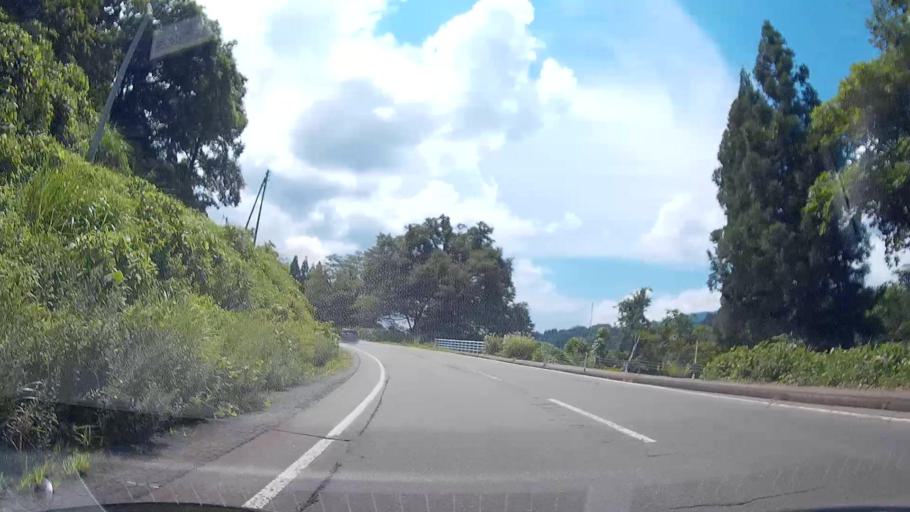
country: JP
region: Niigata
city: Tokamachi
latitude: 37.0024
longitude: 138.6287
